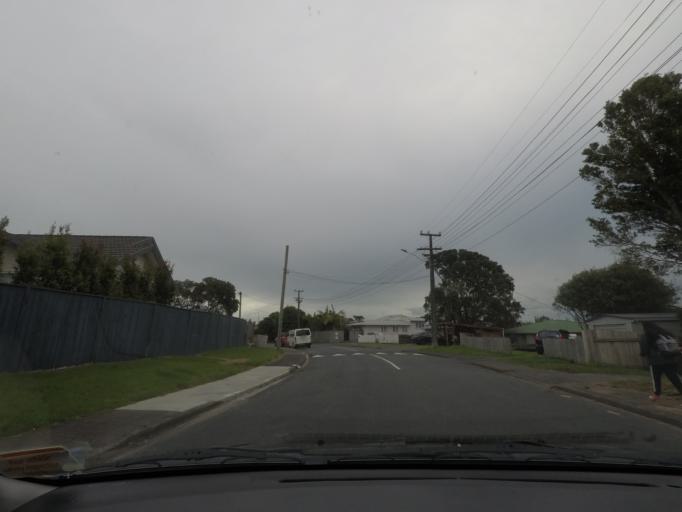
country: NZ
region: Auckland
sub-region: Auckland
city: Rosebank
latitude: -36.8618
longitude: 174.6414
